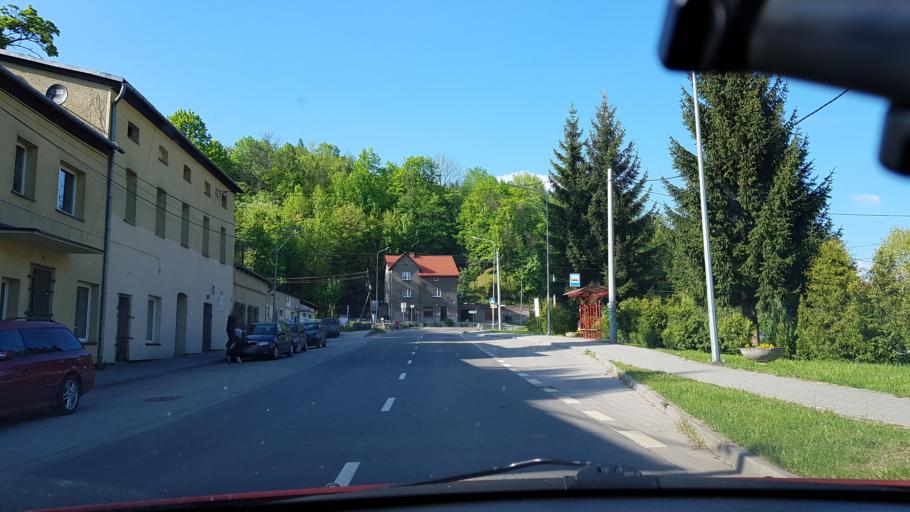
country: PL
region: Lower Silesian Voivodeship
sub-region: Powiat klodzki
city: Nowa Ruda
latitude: 50.5743
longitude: 16.4756
